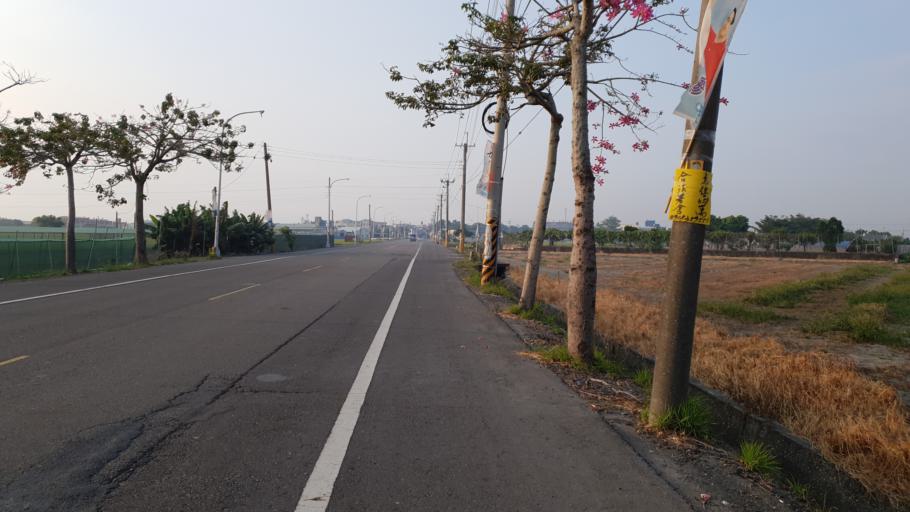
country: TW
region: Taiwan
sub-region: Yunlin
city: Douliu
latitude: 23.7643
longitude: 120.4174
